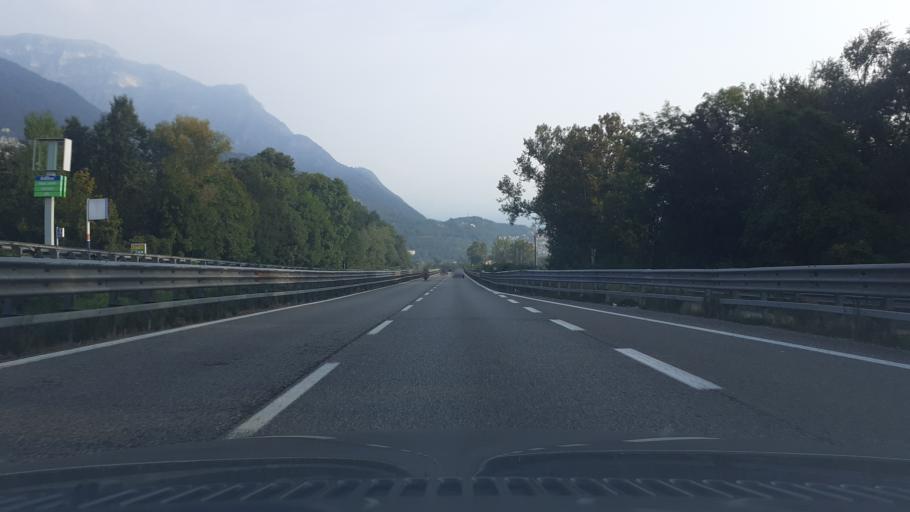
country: IT
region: Lombardy
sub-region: Provincia di Lecco
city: Suello
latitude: 45.8112
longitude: 9.3173
